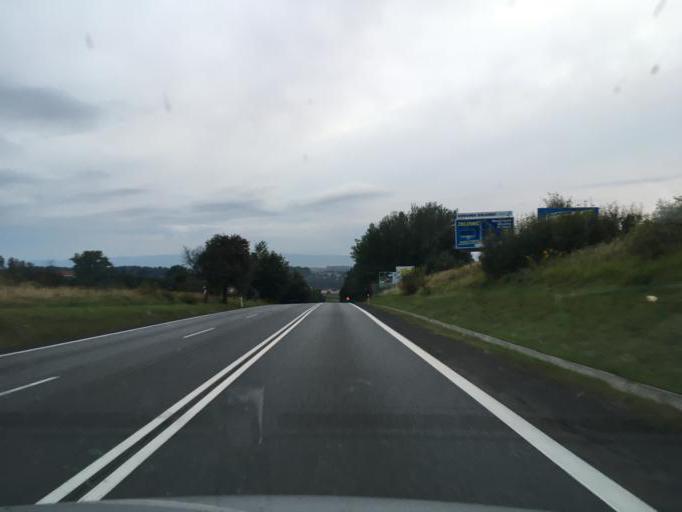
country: PL
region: Lower Silesian Voivodeship
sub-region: Powiat klodzki
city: Klodzko
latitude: 50.4612
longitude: 16.6777
